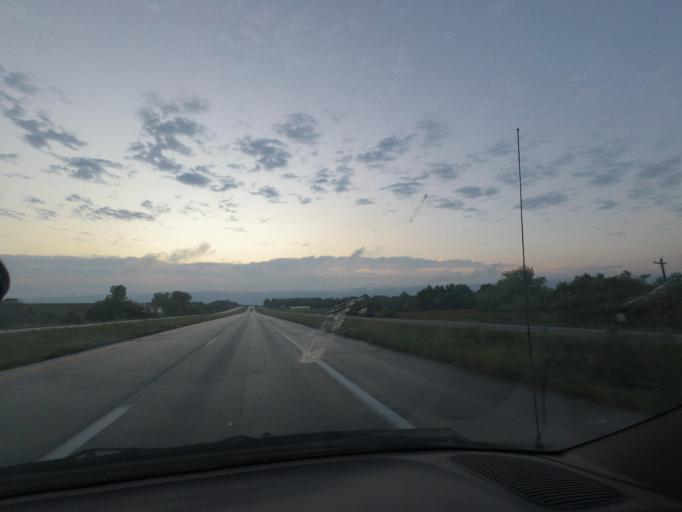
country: US
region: Missouri
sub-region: Macon County
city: Macon
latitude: 39.7489
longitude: -92.5195
